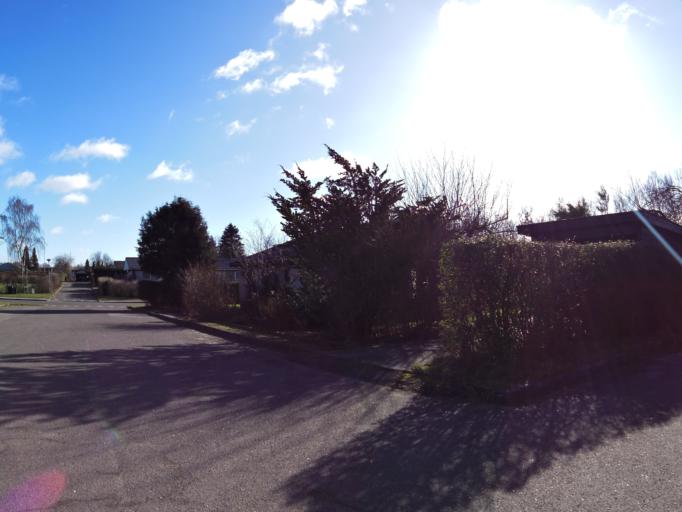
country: DK
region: Central Jutland
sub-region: Arhus Kommune
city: Tranbjerg
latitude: 56.0944
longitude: 10.1306
